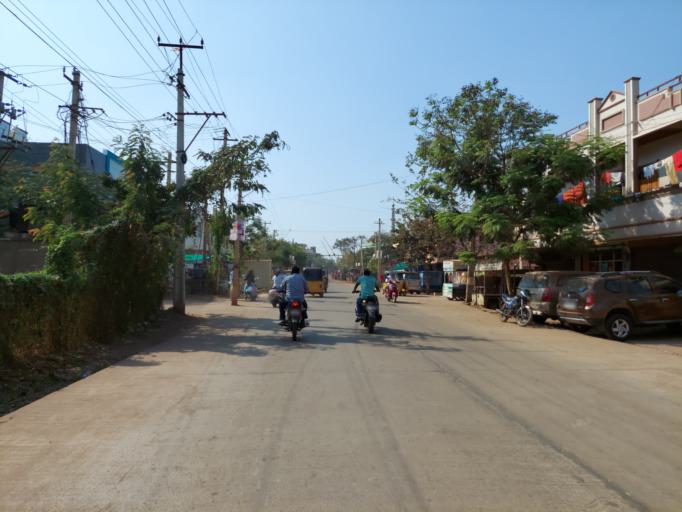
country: IN
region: Telangana
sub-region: Rangareddi
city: Vikarabad
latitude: 17.3380
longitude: 77.8999
